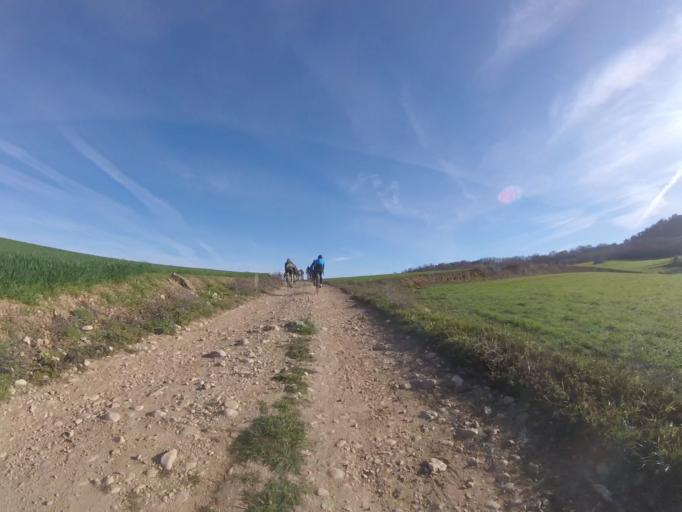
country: ES
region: Navarre
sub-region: Provincia de Navarra
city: Villatuerta
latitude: 42.6628
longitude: -1.9629
